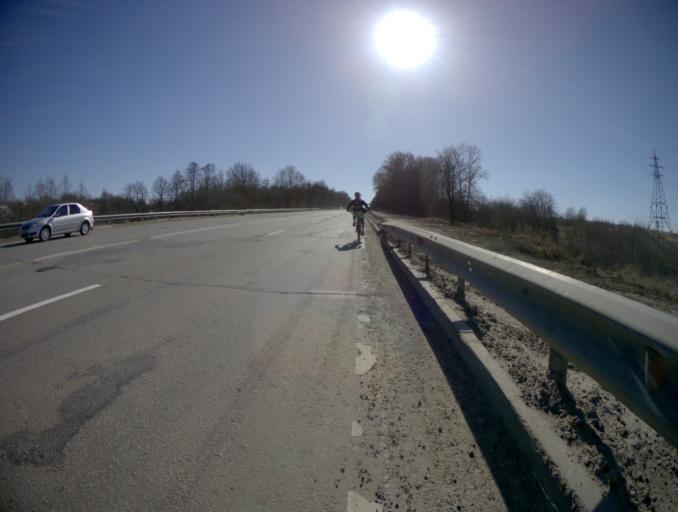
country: RU
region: Vladimir
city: Bogolyubovo
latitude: 56.1812
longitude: 40.5082
